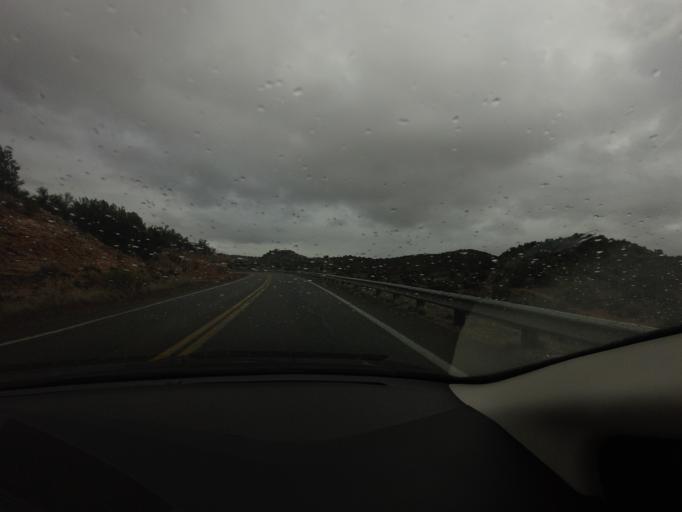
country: US
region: Arizona
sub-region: Yavapai County
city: Cornville
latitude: 34.7013
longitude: -111.8682
